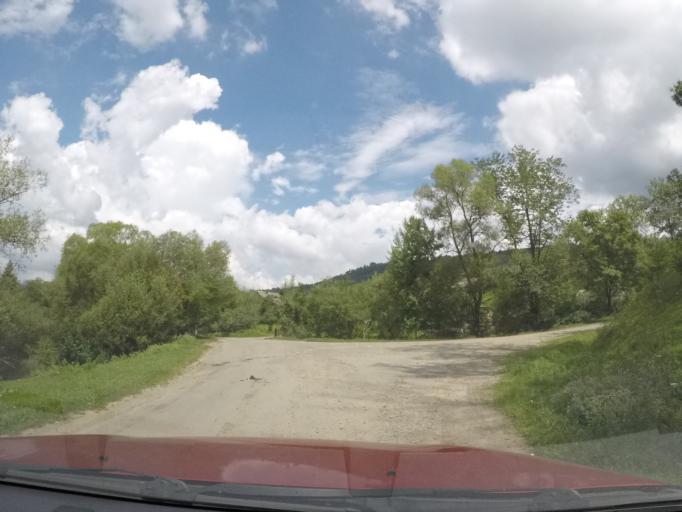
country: UA
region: Zakarpattia
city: Velykyi Bereznyi
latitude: 49.0152
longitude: 22.6211
